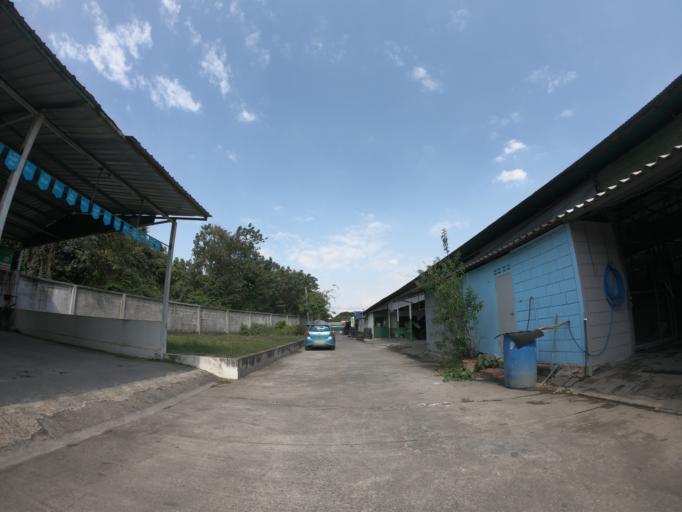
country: TH
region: Chiang Mai
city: Chiang Mai
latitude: 18.8117
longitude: 99.0101
